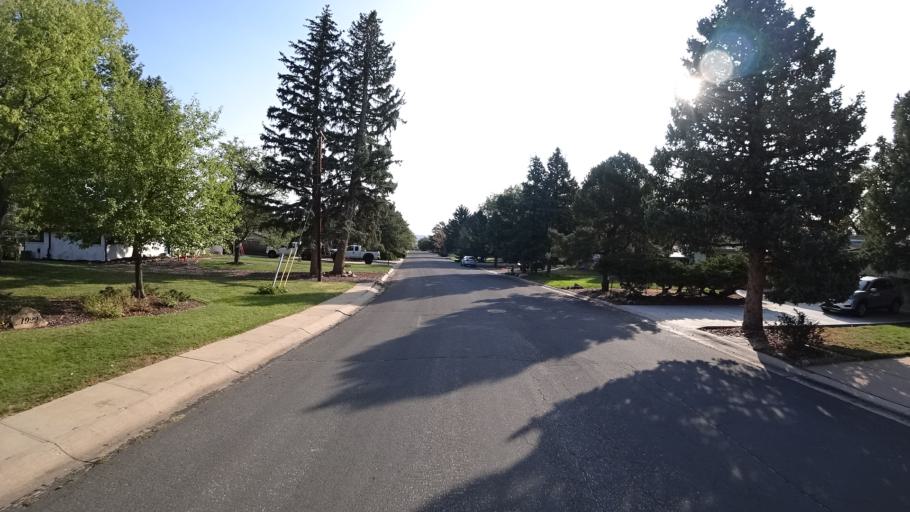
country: US
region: Colorado
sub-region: El Paso County
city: Colorado Springs
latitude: 38.8150
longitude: -104.8574
